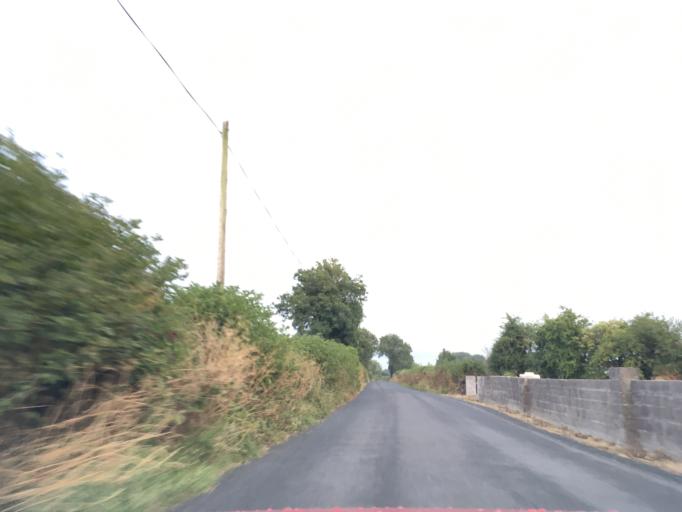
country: IE
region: Munster
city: Cashel
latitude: 52.4717
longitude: -7.9791
